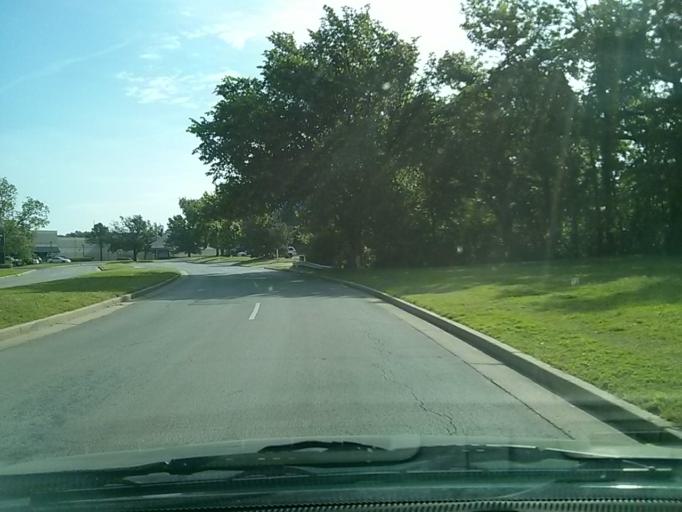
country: US
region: Oklahoma
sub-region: Tulsa County
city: Jenks
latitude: 36.0571
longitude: -95.9611
